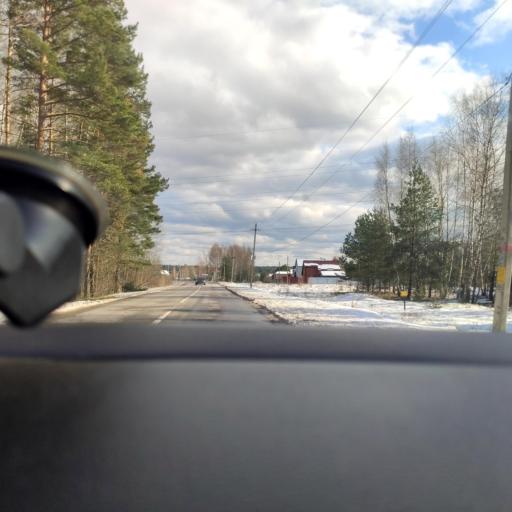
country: RU
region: Moskovskaya
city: Gzhel'
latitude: 55.6343
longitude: 38.4211
